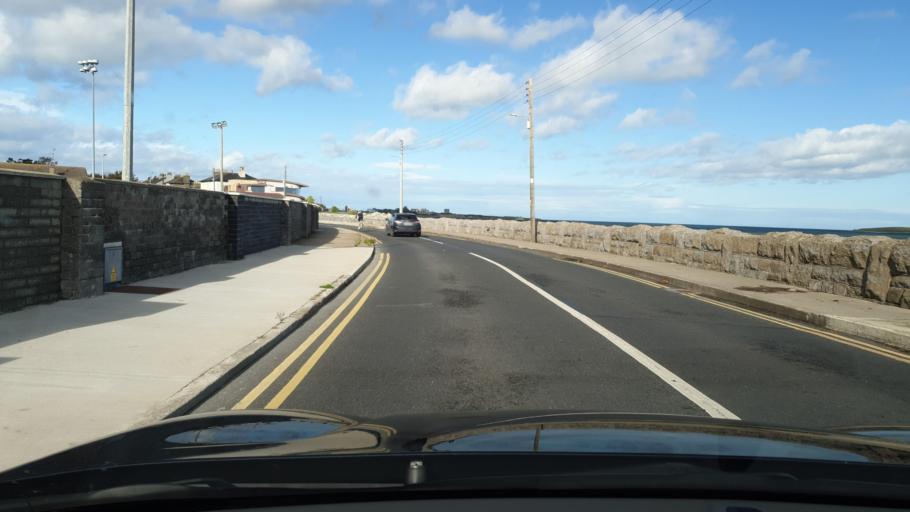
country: IE
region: Leinster
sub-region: Fingal County
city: Skerries
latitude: 53.5714
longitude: -6.1005
